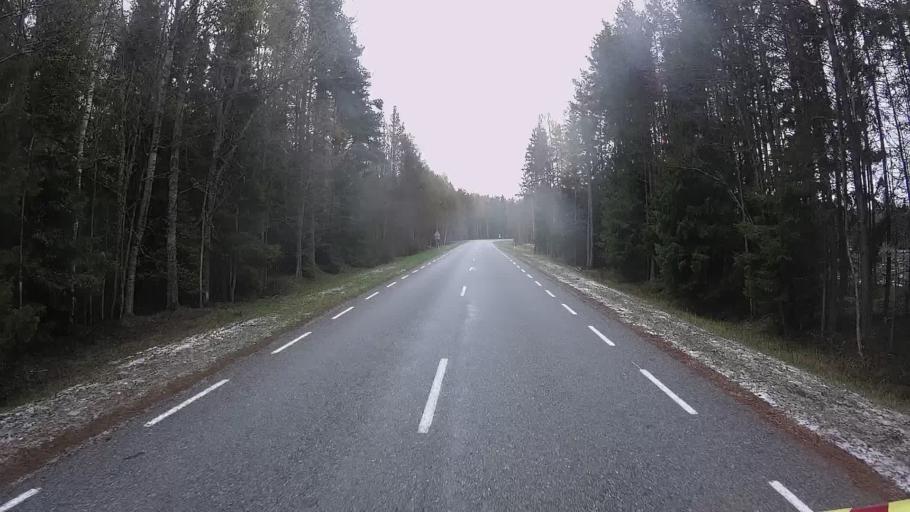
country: EE
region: Hiiumaa
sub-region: Kaerdla linn
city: Kardla
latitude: 59.0405
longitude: 22.6822
